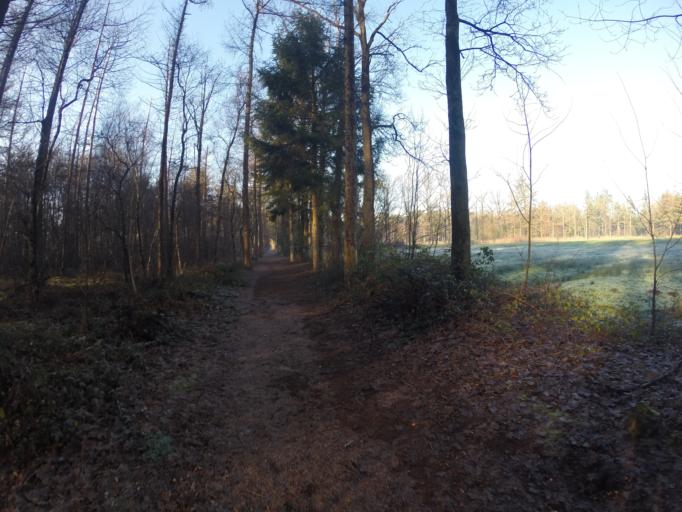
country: BE
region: Flanders
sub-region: Provincie West-Vlaanderen
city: Beernem
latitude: 51.0926
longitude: 3.3313
